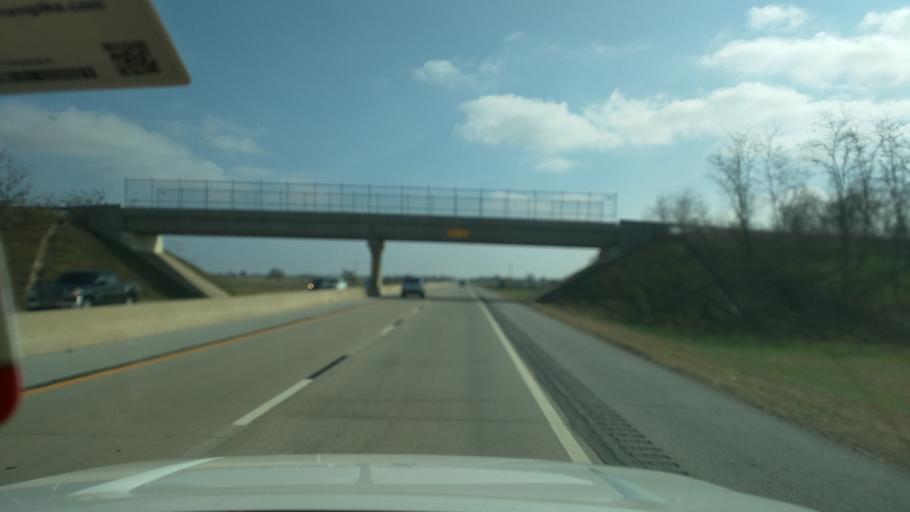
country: US
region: Oklahoma
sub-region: Wagoner County
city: Coweta
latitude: 35.9143
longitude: -95.5511
